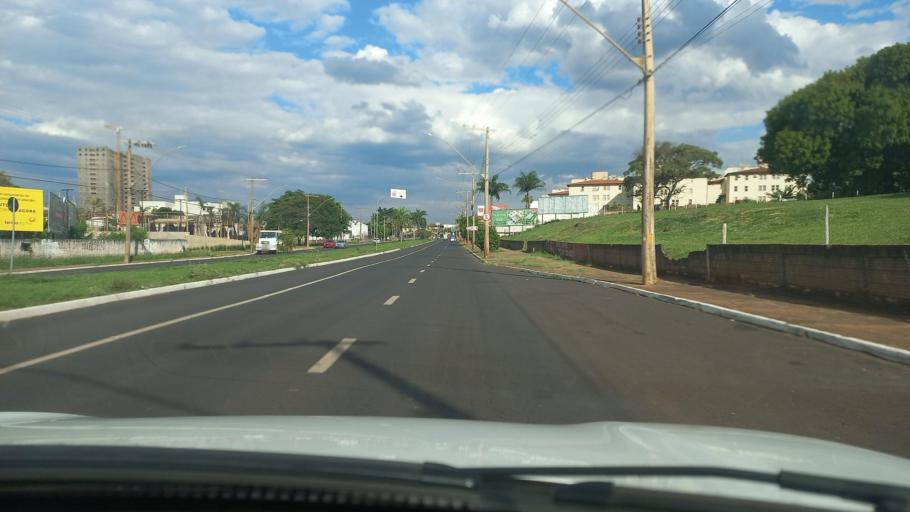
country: BR
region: Minas Gerais
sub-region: Uberaba
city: Uberaba
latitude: -19.7569
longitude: -47.9127
